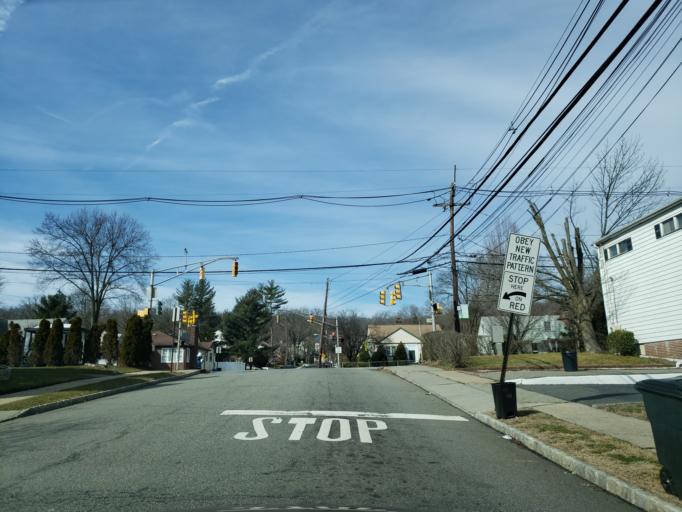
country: US
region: New Jersey
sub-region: Essex County
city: West Orange
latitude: 40.8026
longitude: -74.2640
